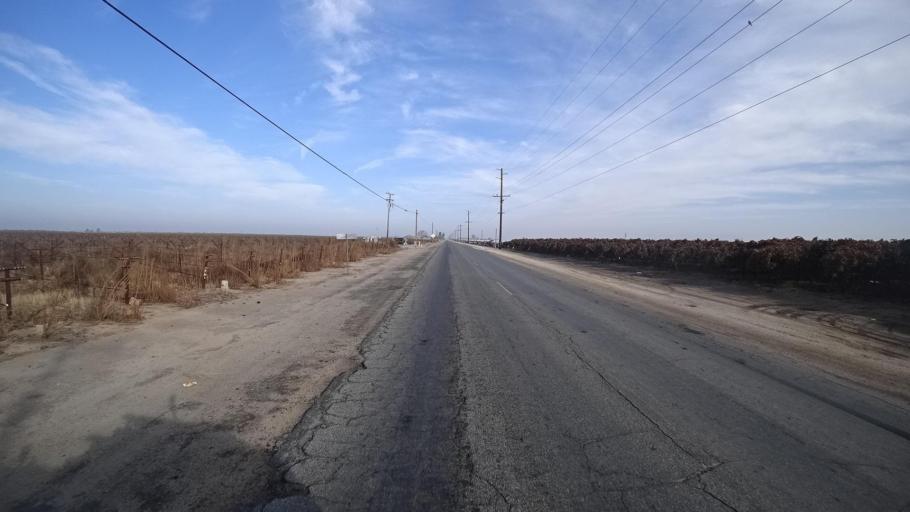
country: US
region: California
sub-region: Kern County
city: Delano
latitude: 35.7479
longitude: -119.2052
